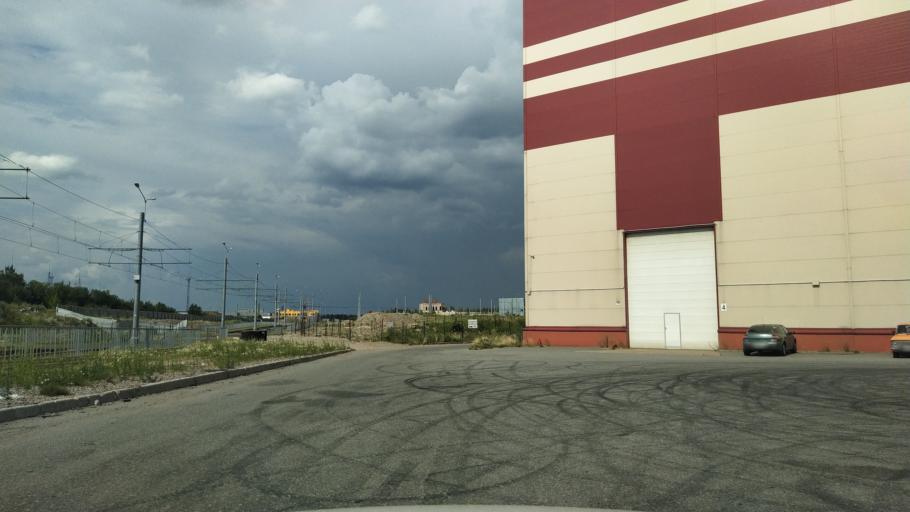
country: RU
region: St.-Petersburg
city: Krasnogvargeisky
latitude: 59.9691
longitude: 30.4633
